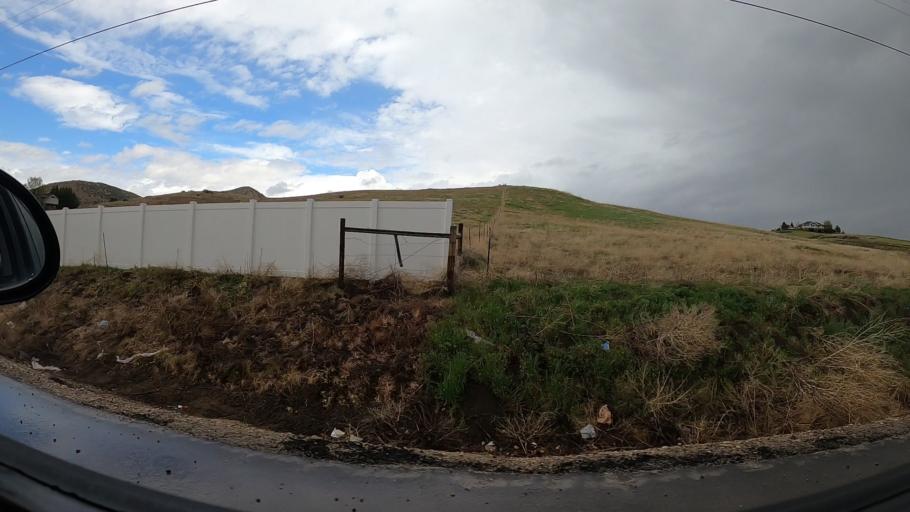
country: US
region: Idaho
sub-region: Ada County
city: Eagle
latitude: 43.7355
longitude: -116.2969
